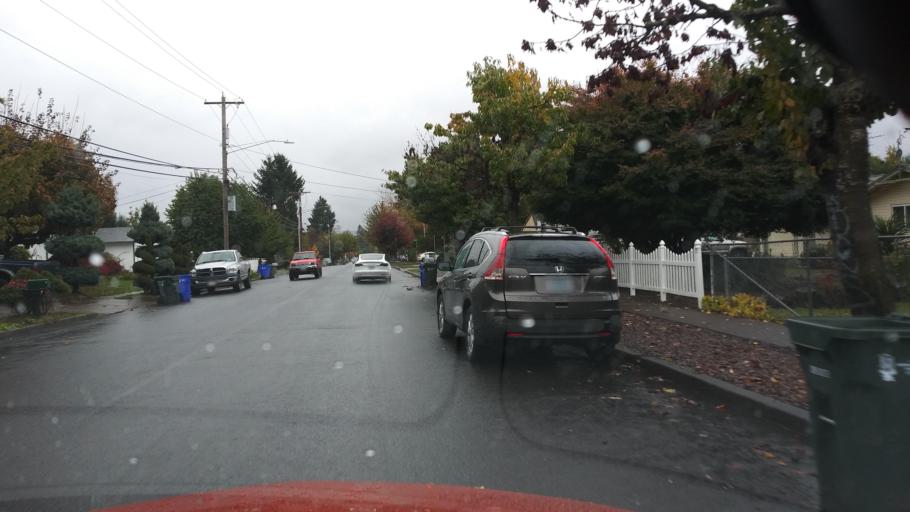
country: US
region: Oregon
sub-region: Washington County
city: Cornelius
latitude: 45.5185
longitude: -123.0665
